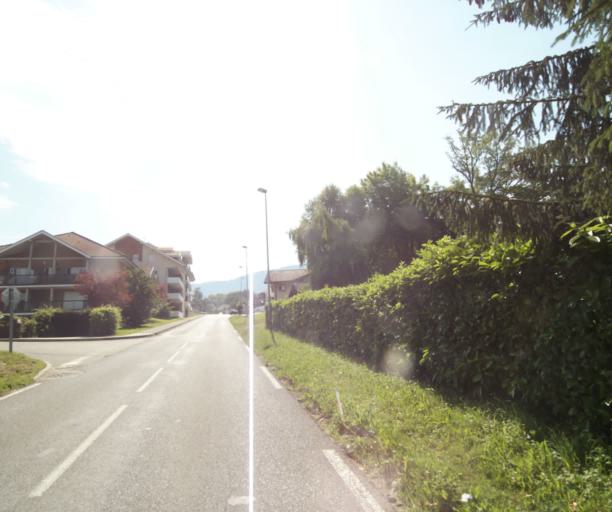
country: FR
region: Rhone-Alpes
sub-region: Departement de la Haute-Savoie
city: Allinges
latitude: 46.3352
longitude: 6.4776
